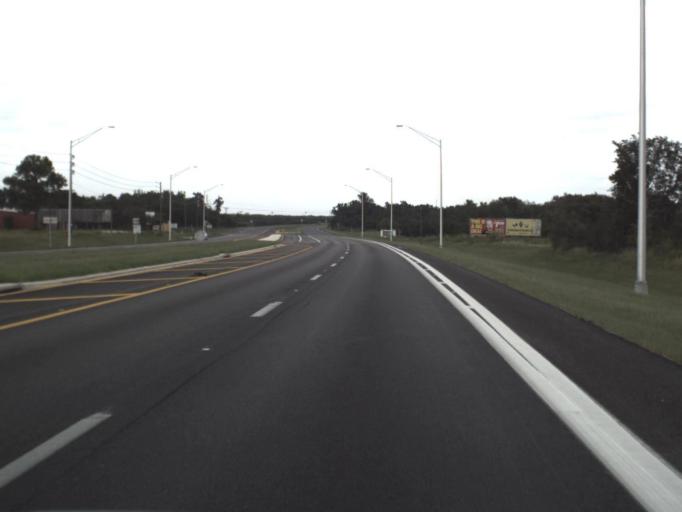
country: US
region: Florida
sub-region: Highlands County
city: Avon Park
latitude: 27.6448
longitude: -81.5282
